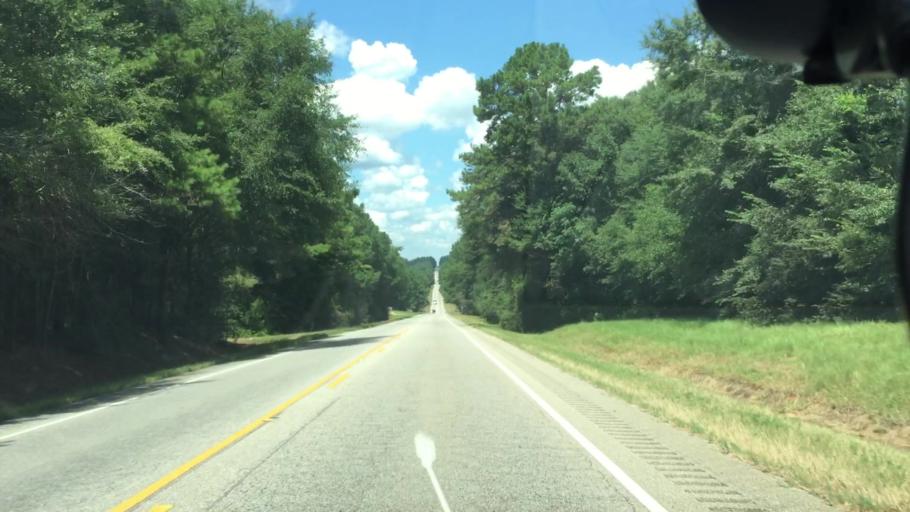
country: US
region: Alabama
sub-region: Coffee County
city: New Brockton
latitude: 31.4334
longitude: -85.8903
